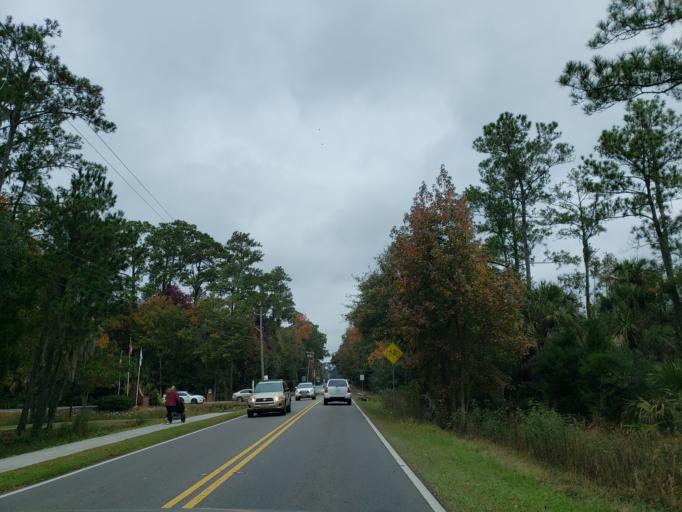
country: US
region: Georgia
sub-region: Chatham County
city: Wilmington Island
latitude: 32.0125
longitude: -80.9743
